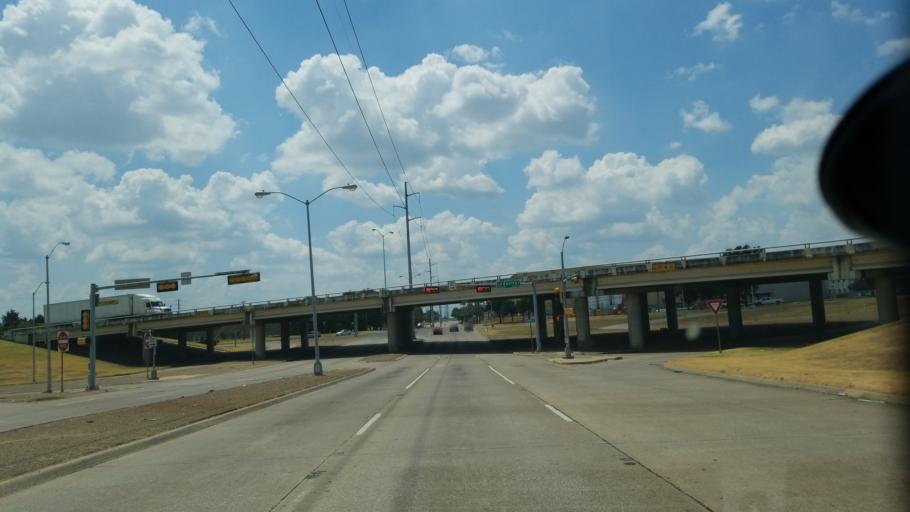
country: US
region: Texas
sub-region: Dallas County
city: Duncanville
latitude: 32.6924
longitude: -96.8915
